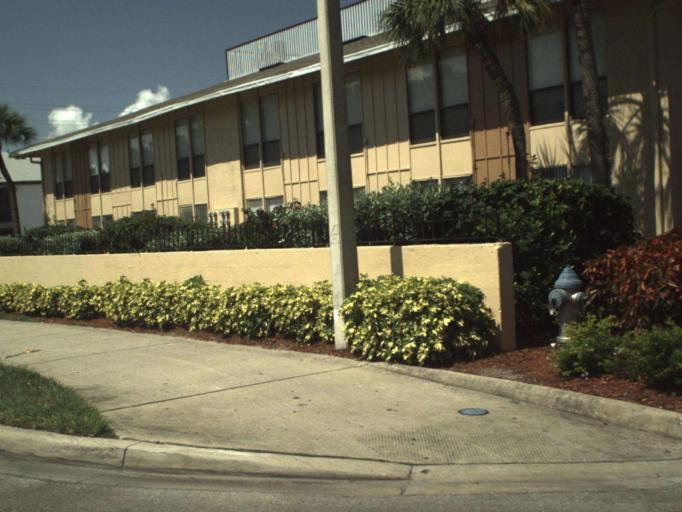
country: US
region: Florida
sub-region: Orange County
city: Conway
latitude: 28.5182
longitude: -81.3311
